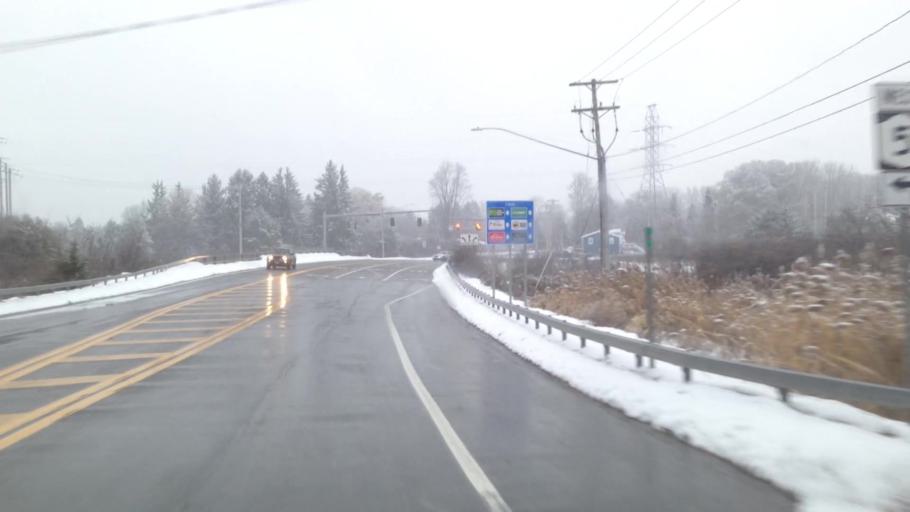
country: US
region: New York
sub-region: Onondaga County
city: Camillus
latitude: 43.0535
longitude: -76.2785
